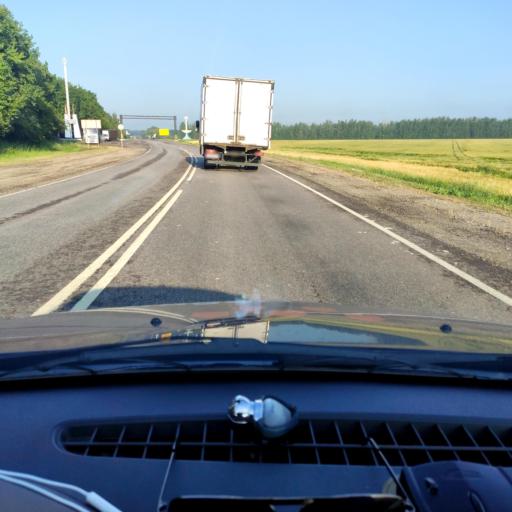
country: RU
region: Lipetsk
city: Izmalkovo
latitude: 52.4376
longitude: 37.8904
